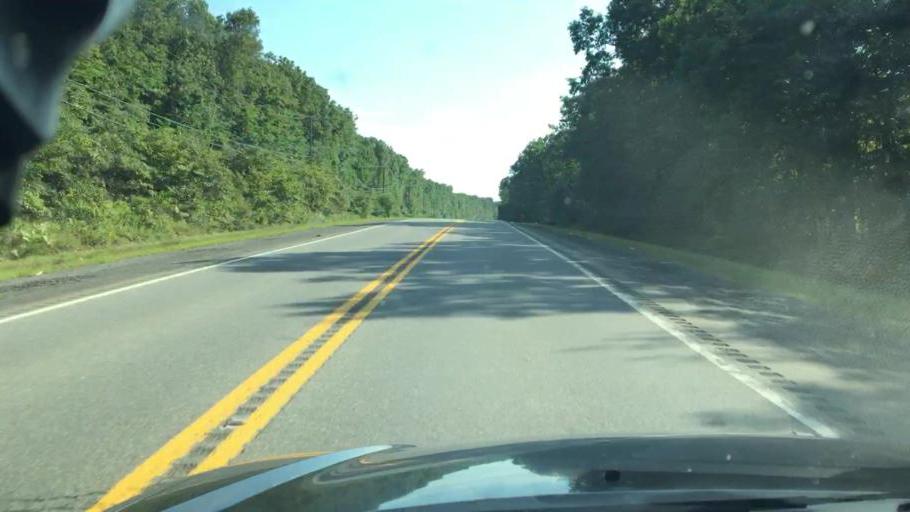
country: US
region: Pennsylvania
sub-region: Carbon County
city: Jim Thorpe
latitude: 40.9222
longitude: -75.6659
